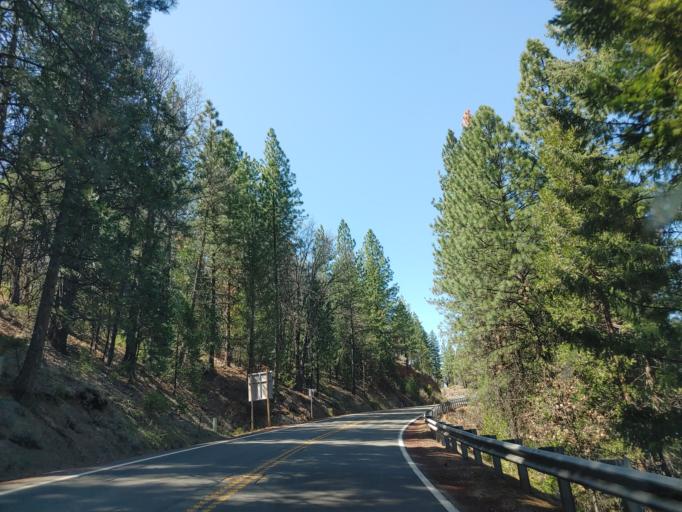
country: US
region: California
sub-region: Shasta County
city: Burney
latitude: 41.0152
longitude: -121.6287
